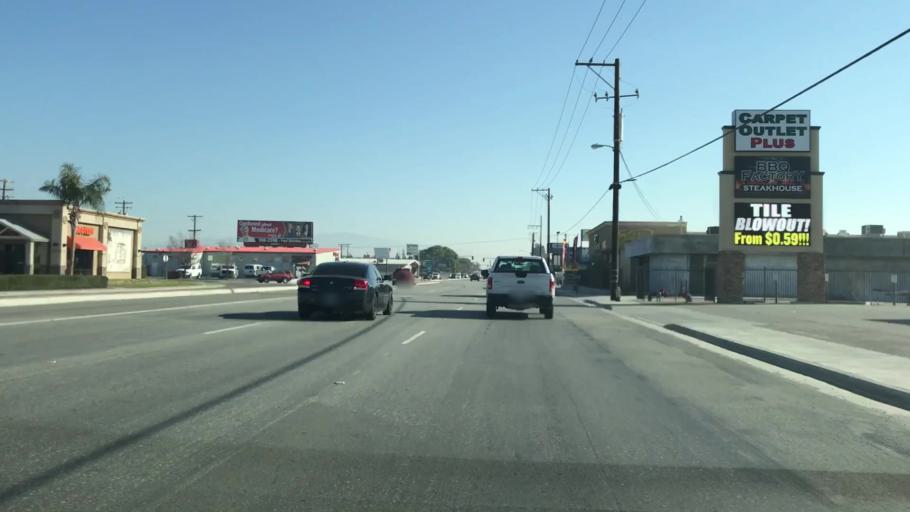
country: US
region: California
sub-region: Kern County
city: Bakersfield
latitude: 35.3832
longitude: -119.0554
